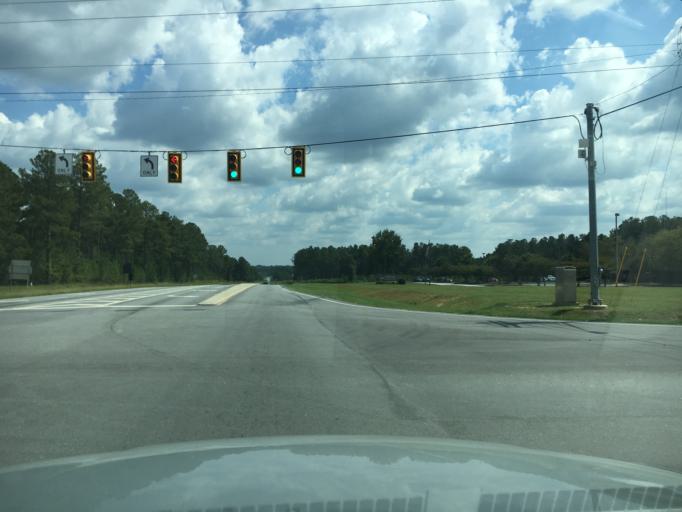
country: US
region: South Carolina
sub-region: Greenwood County
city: Greenwood
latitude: 34.1583
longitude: -82.1761
